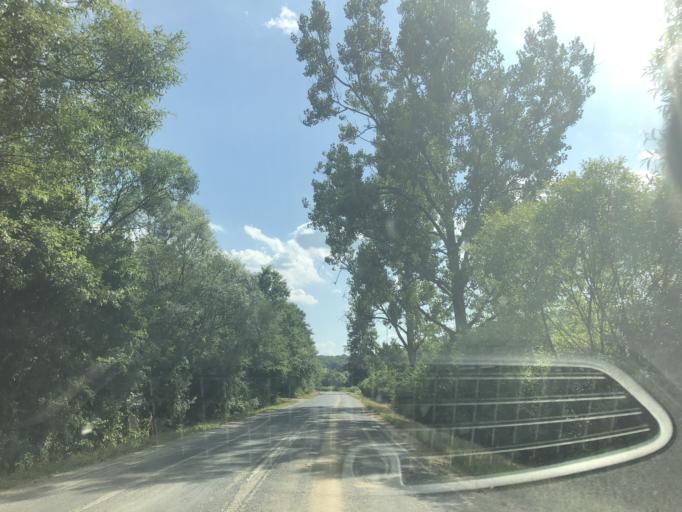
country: HU
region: Borsod-Abauj-Zemplen
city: Szendro
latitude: 48.4479
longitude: 20.7982
